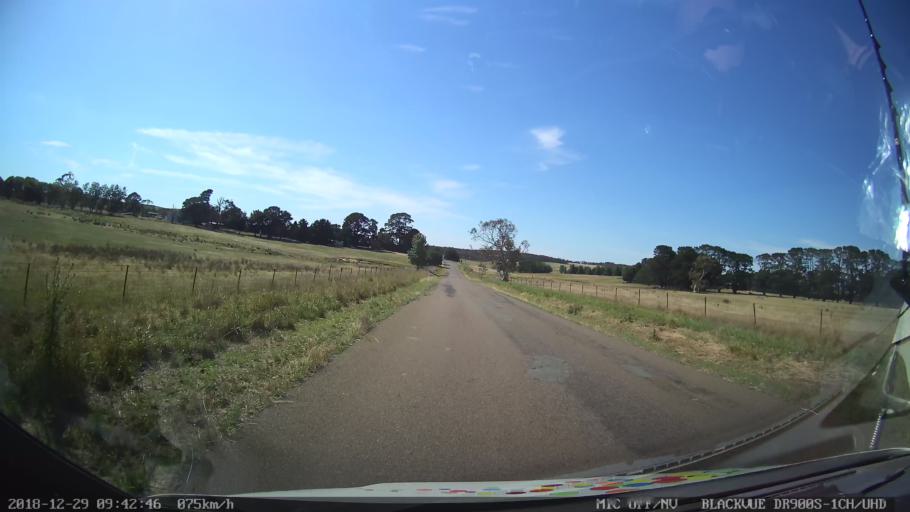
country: AU
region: New South Wales
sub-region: Upper Lachlan Shire
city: Crookwell
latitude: -34.6732
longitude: 149.4222
